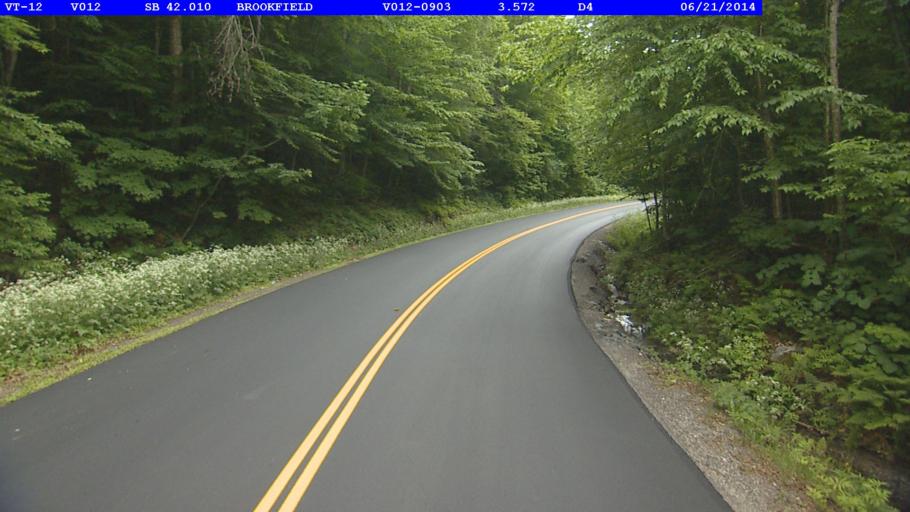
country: US
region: Vermont
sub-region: Washington County
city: Northfield
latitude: 44.0534
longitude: -72.6412
